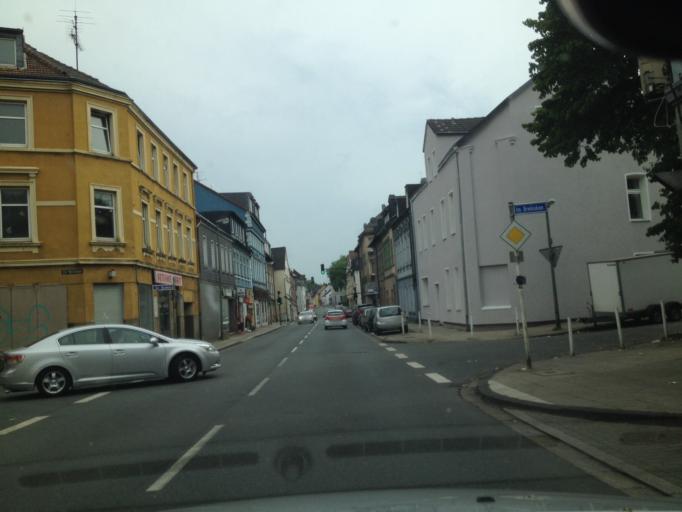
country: DE
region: North Rhine-Westphalia
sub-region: Regierungsbezirk Dusseldorf
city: Essen
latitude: 51.4582
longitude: 7.0781
